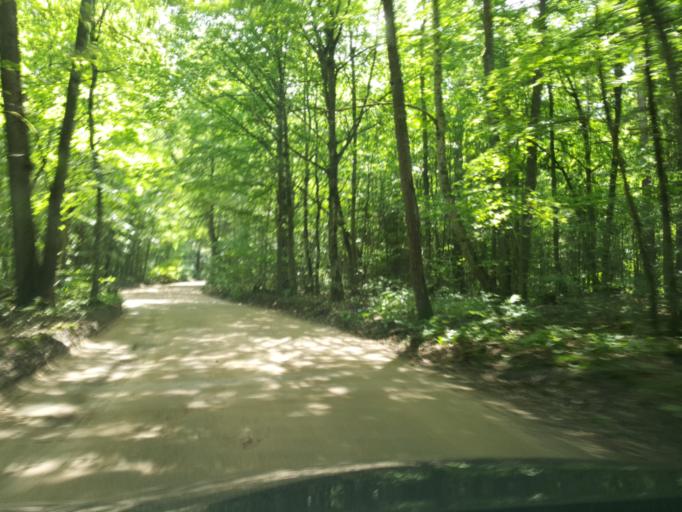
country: LT
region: Alytaus apskritis
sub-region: Alytus
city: Alytus
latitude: 54.3765
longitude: 24.0464
